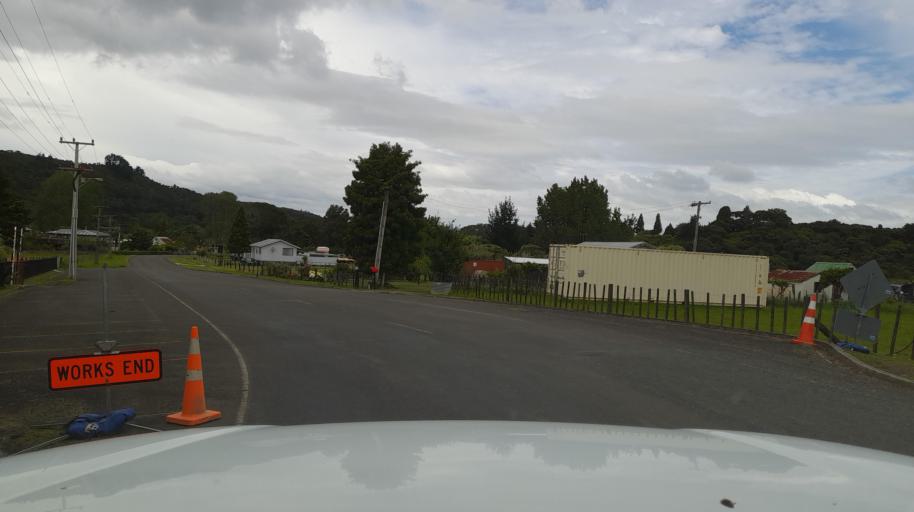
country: NZ
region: Northland
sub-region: Far North District
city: Kaitaia
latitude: -35.3768
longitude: 173.3809
